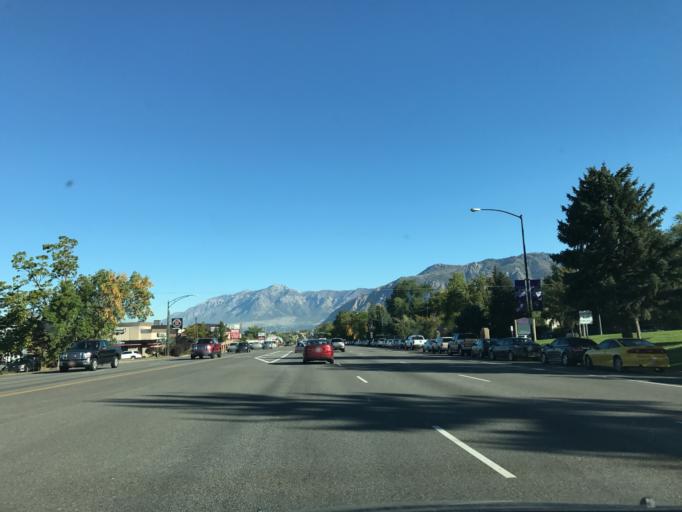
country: US
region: Utah
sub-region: Weber County
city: South Ogden
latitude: 41.1949
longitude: -111.9487
